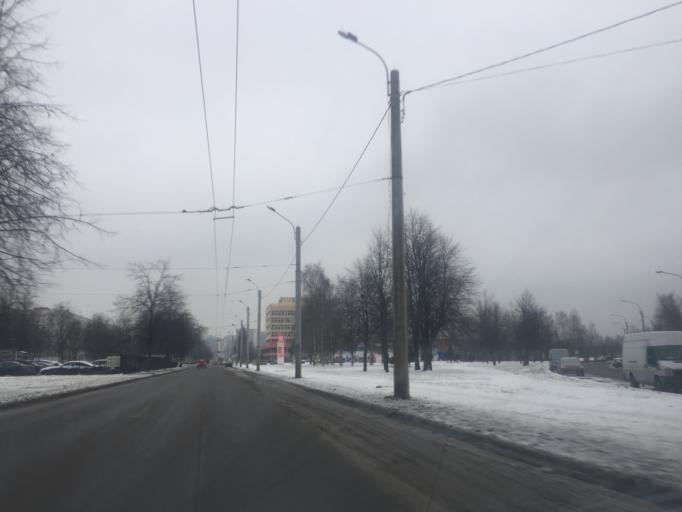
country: RU
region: St.-Petersburg
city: Grazhdanka
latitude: 60.0382
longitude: 30.4234
